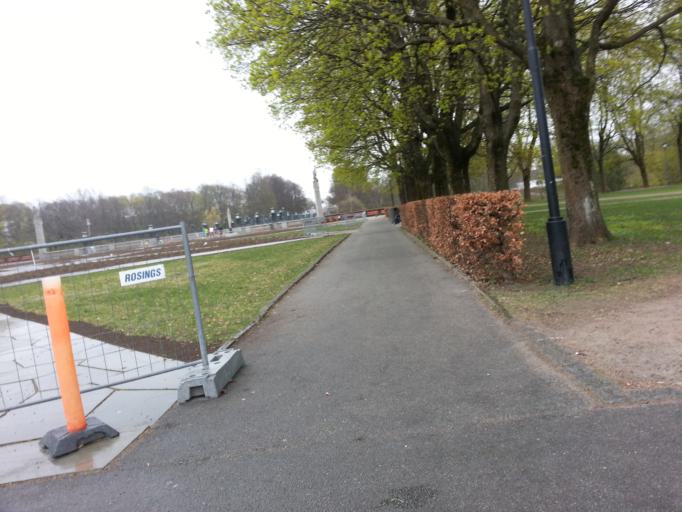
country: NO
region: Oslo
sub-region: Oslo
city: Sjolyststranda
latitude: 59.9265
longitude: 10.7014
